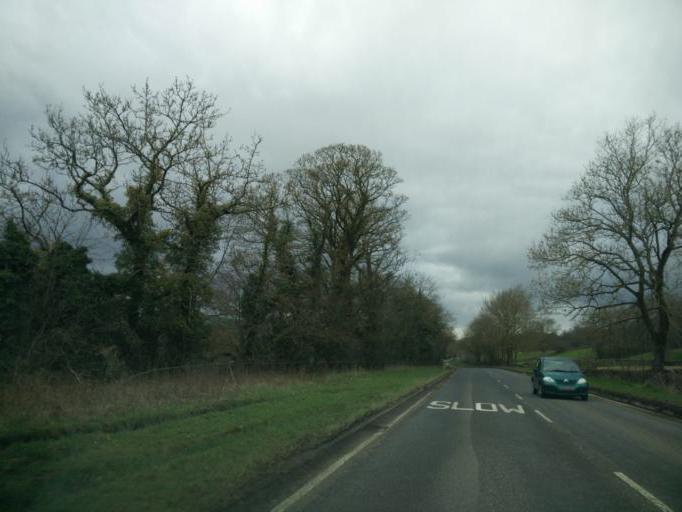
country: GB
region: England
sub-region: County Durham
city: Wolsingham
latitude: 54.7273
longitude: -1.9429
